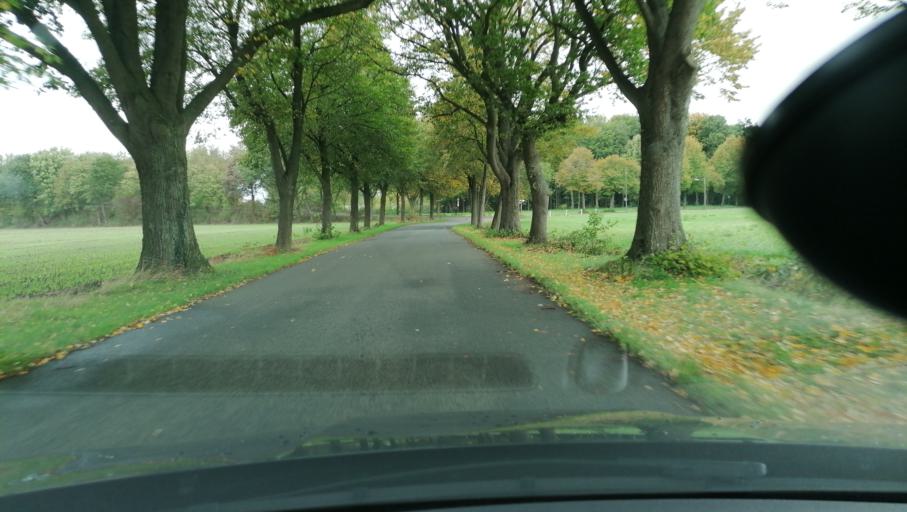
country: DE
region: North Rhine-Westphalia
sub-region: Regierungsbezirk Munster
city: Recklinghausen
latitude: 51.6356
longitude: 7.1732
